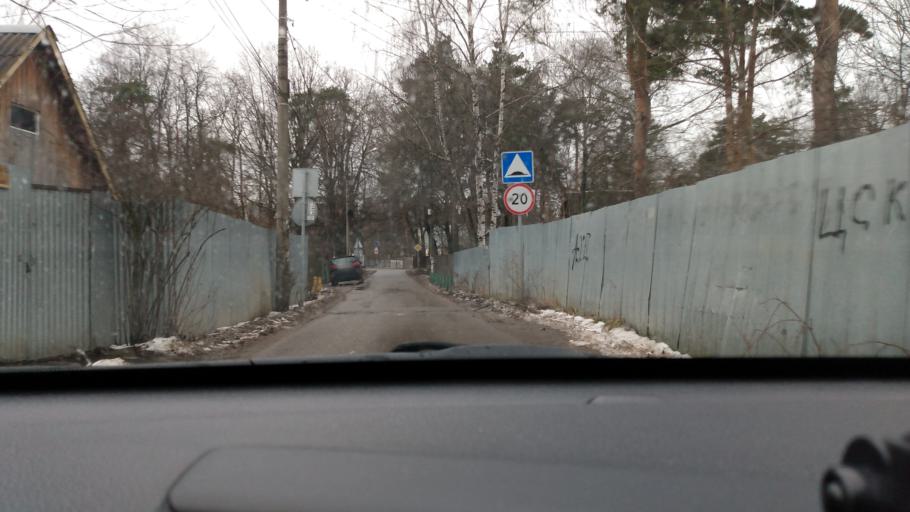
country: RU
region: Moskovskaya
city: Druzhba
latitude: 55.8988
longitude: 37.7440
